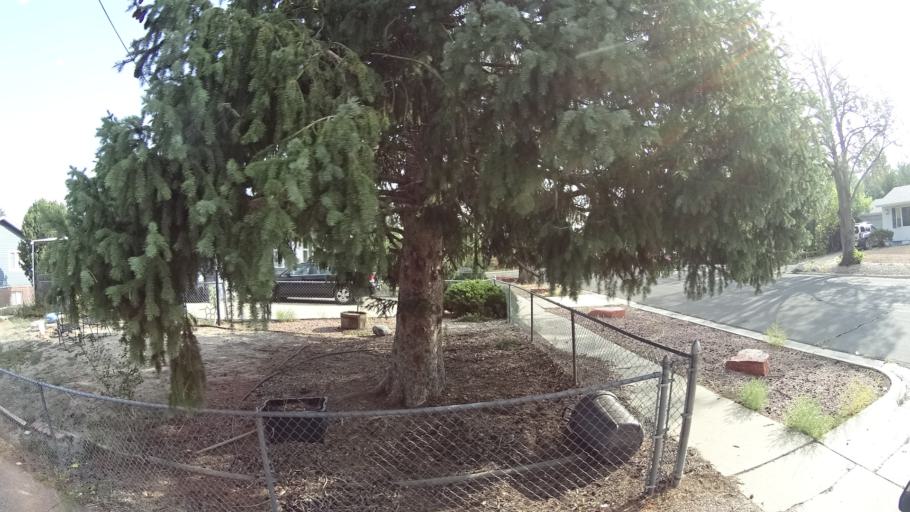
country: US
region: Colorado
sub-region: El Paso County
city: Colorado Springs
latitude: 38.8529
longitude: -104.7790
